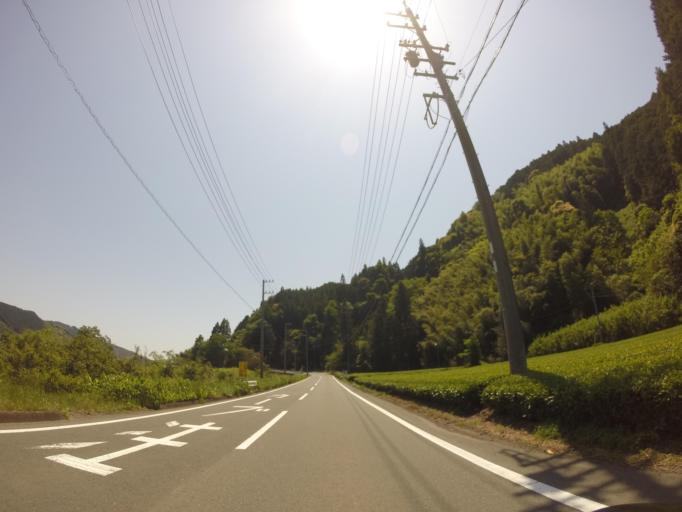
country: JP
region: Shizuoka
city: Shizuoka-shi
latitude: 34.9903
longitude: 138.2893
